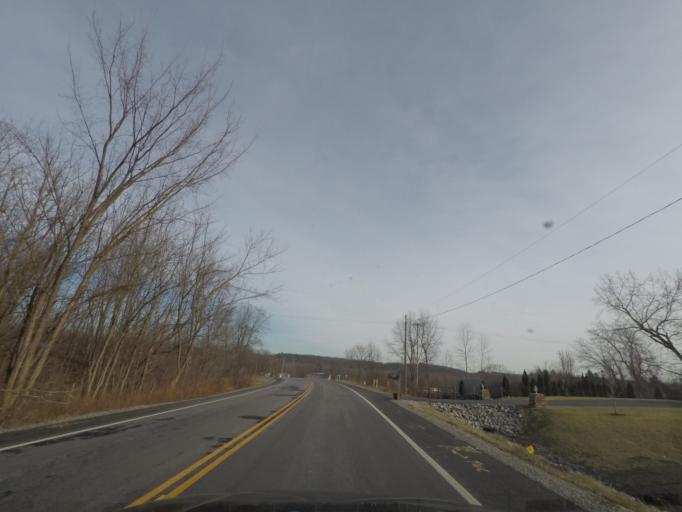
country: US
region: New York
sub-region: Saratoga County
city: Mechanicville
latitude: 42.8610
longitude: -73.6831
